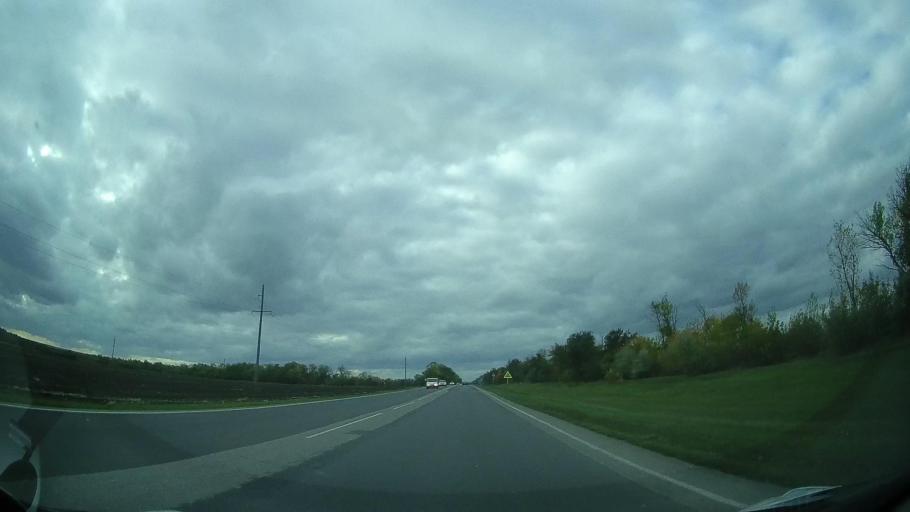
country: RU
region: Rostov
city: Mechetinskaya
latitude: 46.7948
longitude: 40.3816
